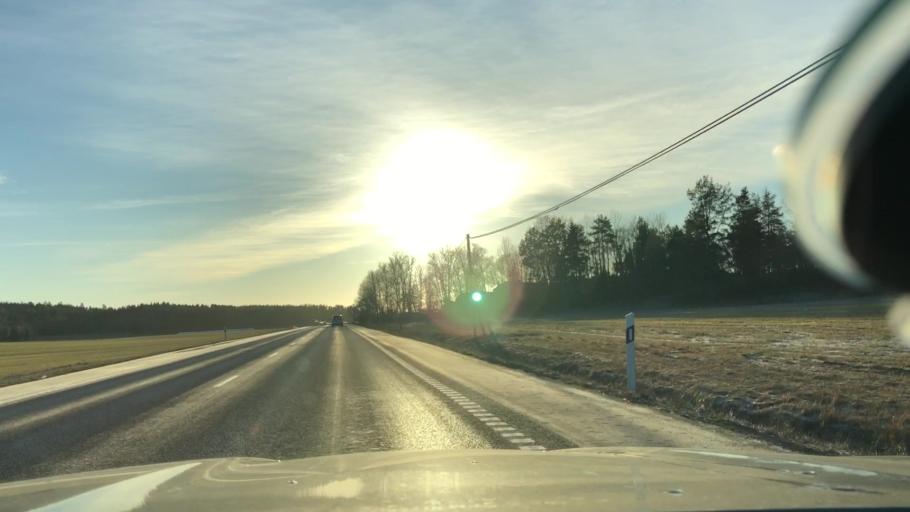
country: SE
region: Soedermanland
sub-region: Trosa Kommun
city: Vagnharad
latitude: 59.0312
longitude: 17.5965
